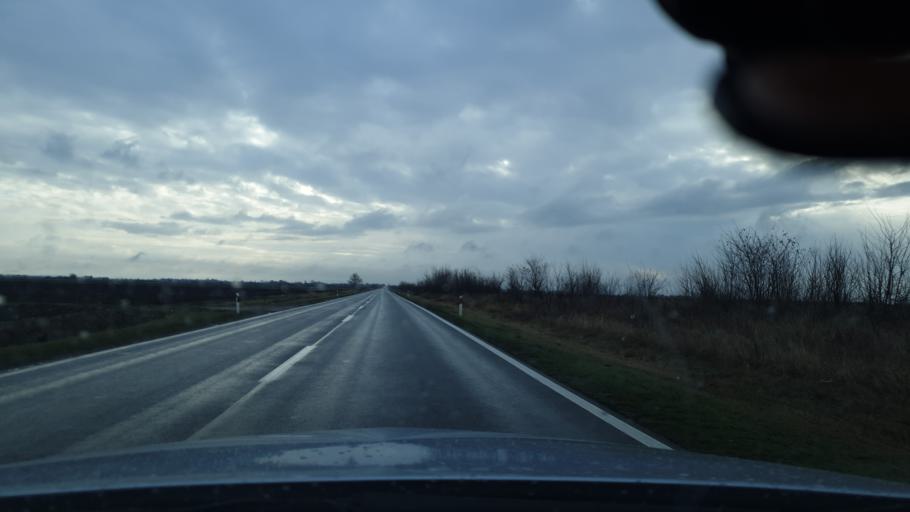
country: RS
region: Autonomna Pokrajina Vojvodina
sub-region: Juznobanatski Okrug
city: Kovin
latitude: 44.7814
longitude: 20.9296
